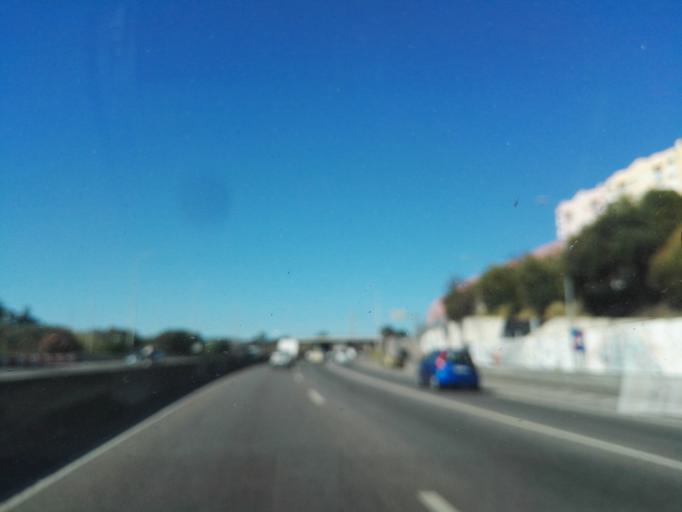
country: PT
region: Lisbon
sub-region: Sintra
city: Cacem
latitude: 38.7666
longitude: -9.3126
